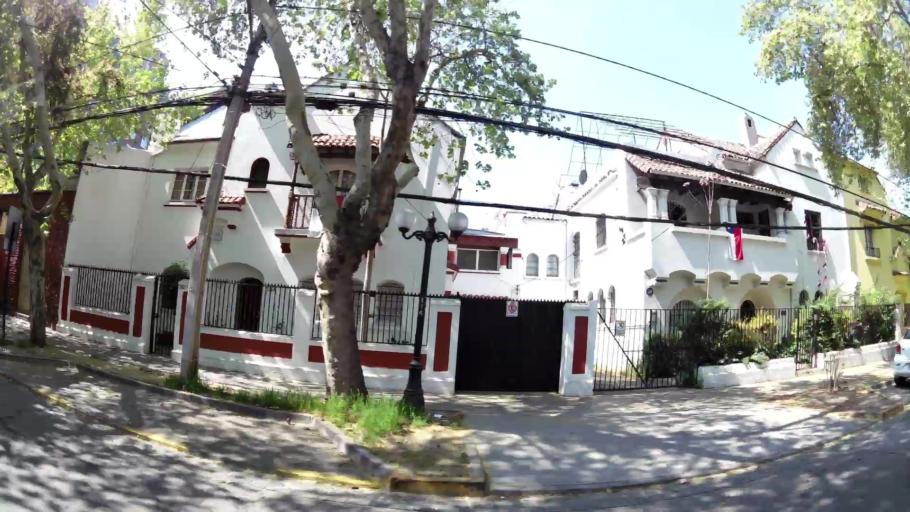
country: CL
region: Santiago Metropolitan
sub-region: Provincia de Santiago
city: Santiago
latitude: -33.4361
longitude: -70.6283
